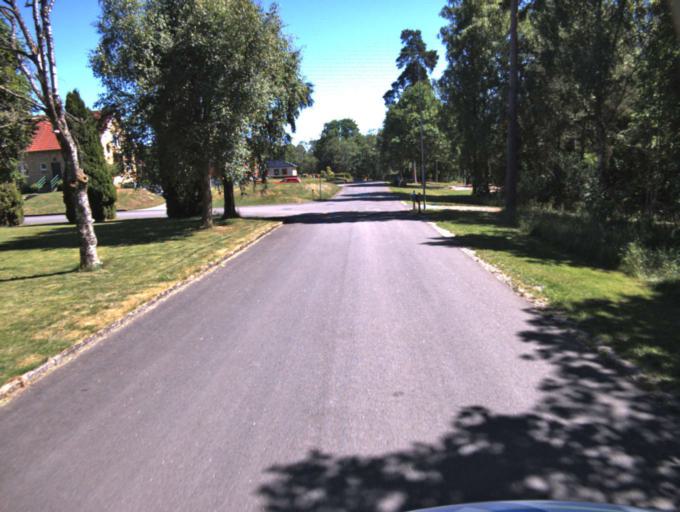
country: SE
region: Vaestra Goetaland
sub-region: Ulricehamns Kommun
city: Ulricehamn
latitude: 57.6653
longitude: 13.4241
